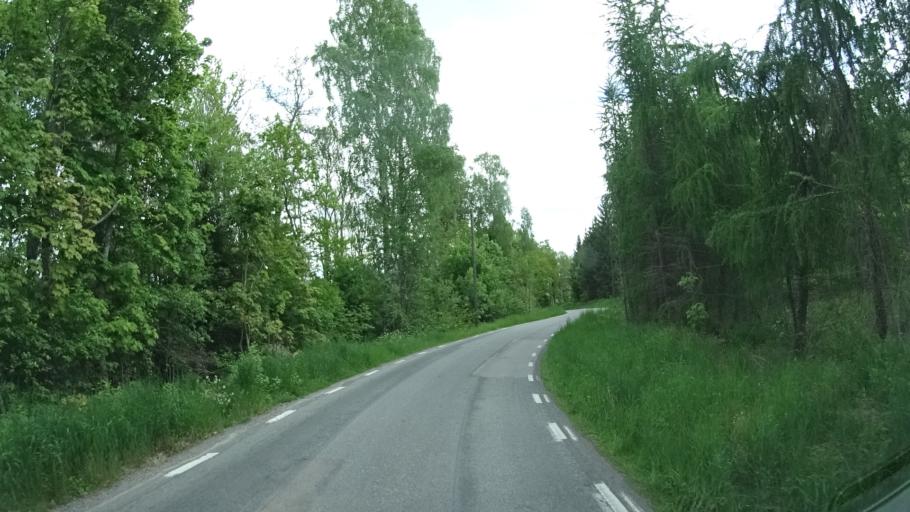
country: SE
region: OEstergoetland
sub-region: Finspangs Kommun
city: Finspang
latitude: 58.5968
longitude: 15.7733
